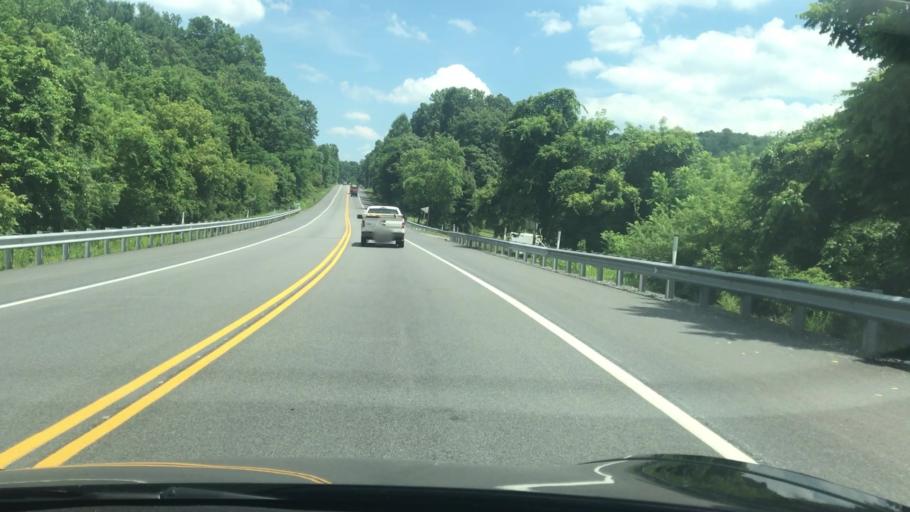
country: US
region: Pennsylvania
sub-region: York County
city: Valley Green
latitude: 40.1309
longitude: -76.8175
